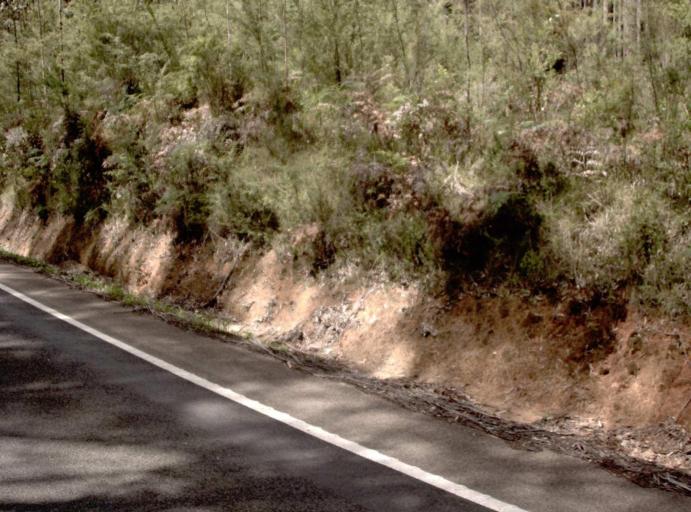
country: AU
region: New South Wales
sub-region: Bombala
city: Bombala
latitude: -37.5389
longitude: 149.3679
